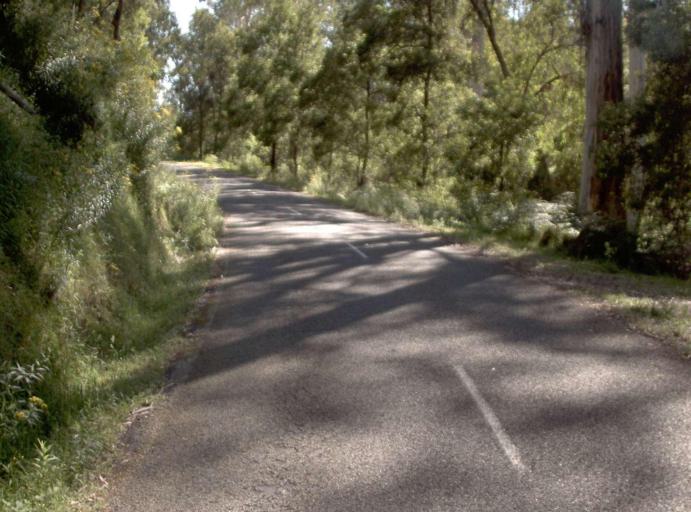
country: AU
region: New South Wales
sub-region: Bombala
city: Bombala
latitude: -37.3528
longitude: 148.6919
